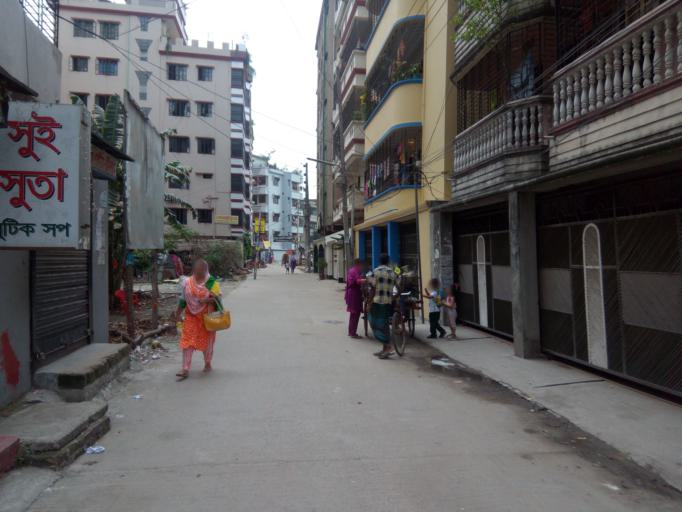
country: BD
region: Dhaka
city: Paltan
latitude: 23.7646
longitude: 90.4142
